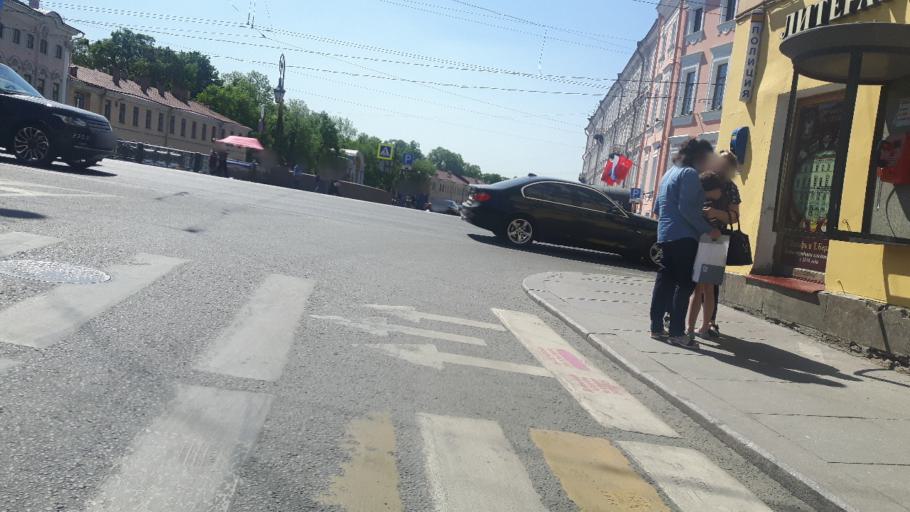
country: RU
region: St.-Petersburg
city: Saint Petersburg
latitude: 59.9363
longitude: 30.3193
